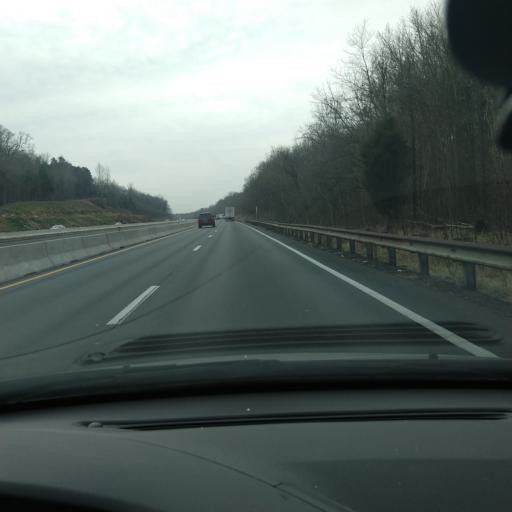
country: US
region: North Carolina
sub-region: Rowan County
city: Landis
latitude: 35.5211
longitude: -80.5713
